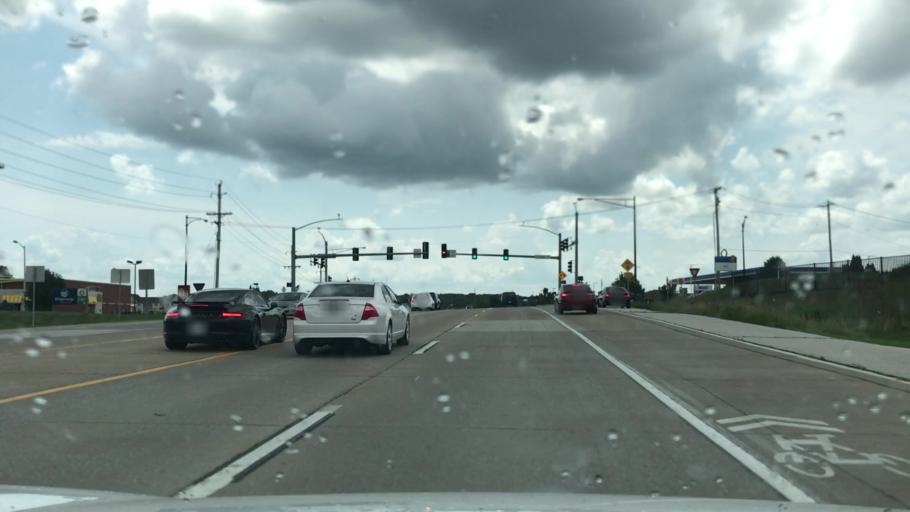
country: US
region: Missouri
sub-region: Saint Charles County
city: Weldon Spring
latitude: 38.7224
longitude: -90.6996
